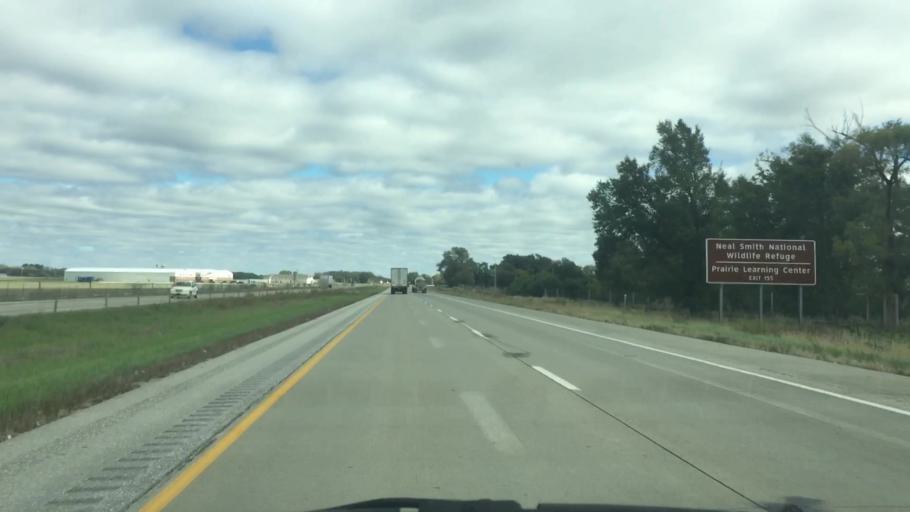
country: US
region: Iowa
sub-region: Jasper County
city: Colfax
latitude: 41.6885
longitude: -93.2626
